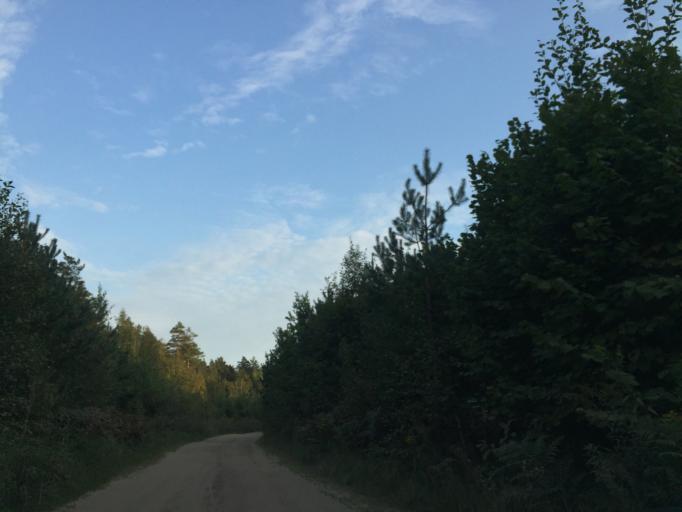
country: LV
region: Baldone
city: Baldone
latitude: 56.7642
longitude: 24.4080
